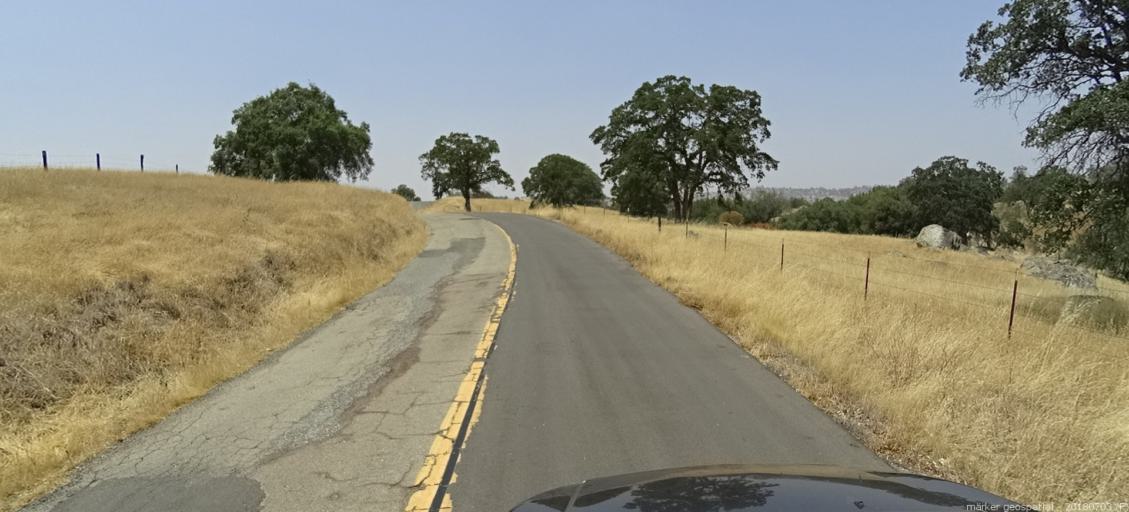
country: US
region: California
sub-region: Madera County
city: Yosemite Lakes
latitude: 37.0566
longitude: -119.7064
